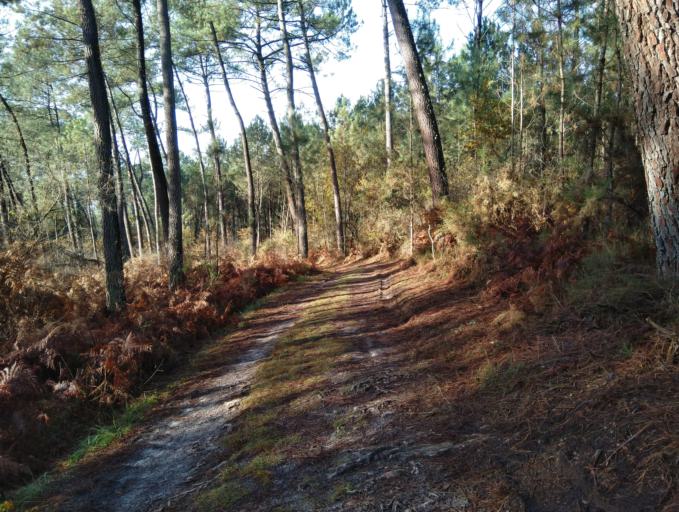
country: FR
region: Aquitaine
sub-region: Departement des Landes
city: Mees
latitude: 43.7056
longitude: -1.1254
